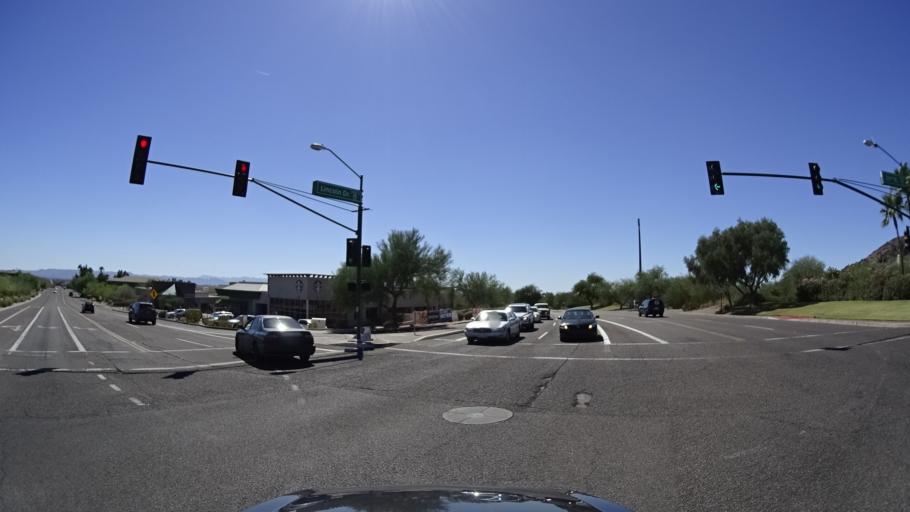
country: US
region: Arizona
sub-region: Maricopa County
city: Paradise Valley
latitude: 33.5318
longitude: -112.0128
